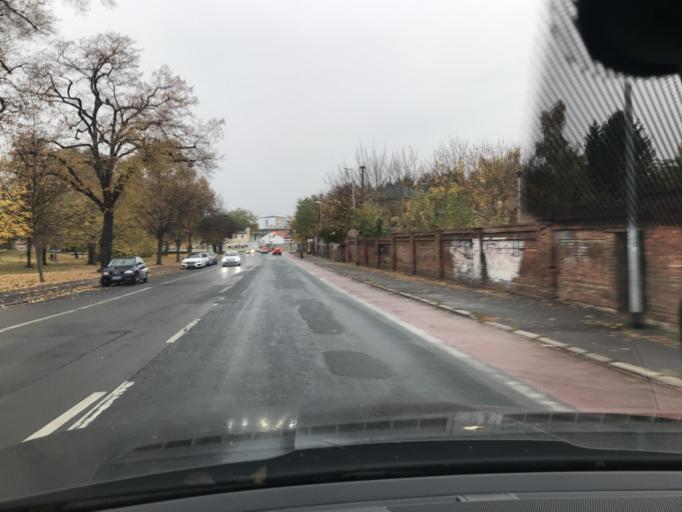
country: DE
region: Saxony-Anhalt
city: Halberstadt
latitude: 51.8981
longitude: 11.0575
